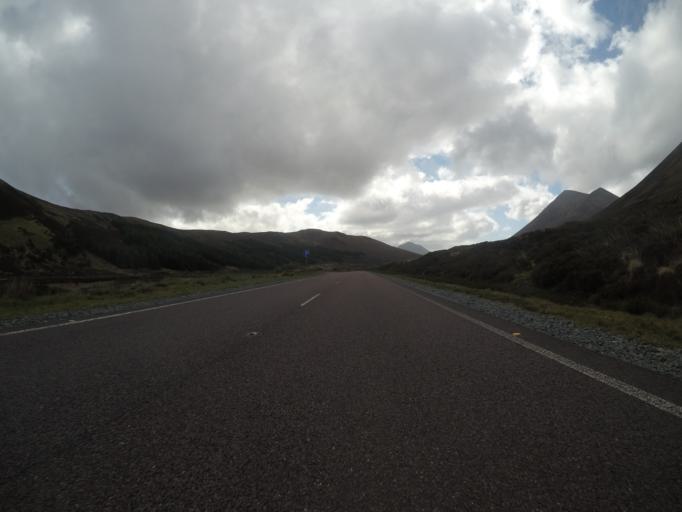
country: GB
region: Scotland
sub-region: Highland
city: Portree
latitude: 57.3029
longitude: -6.0904
